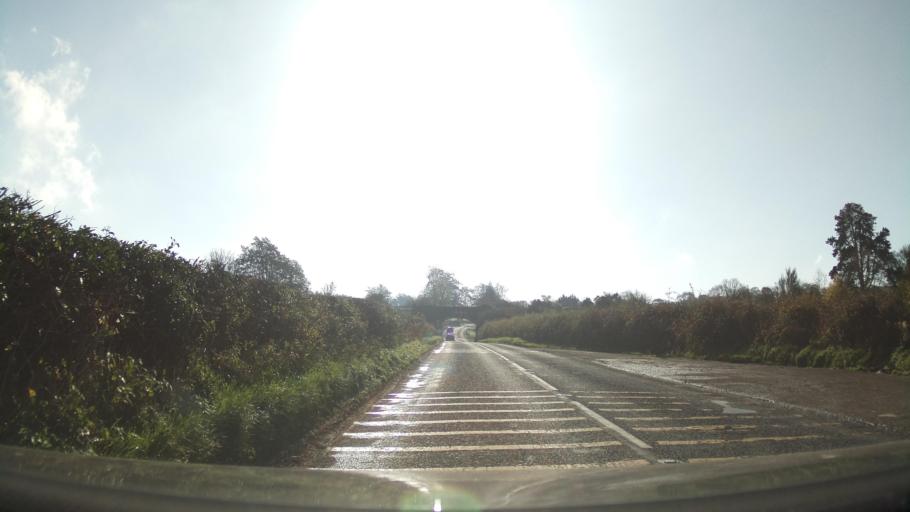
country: GB
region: England
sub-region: Somerset
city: Bruton
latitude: 51.1712
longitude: -2.4145
